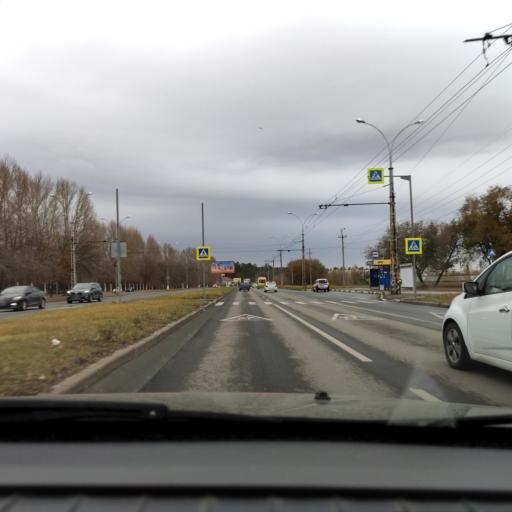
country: RU
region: Samara
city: Tol'yatti
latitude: 53.5032
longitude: 49.2993
